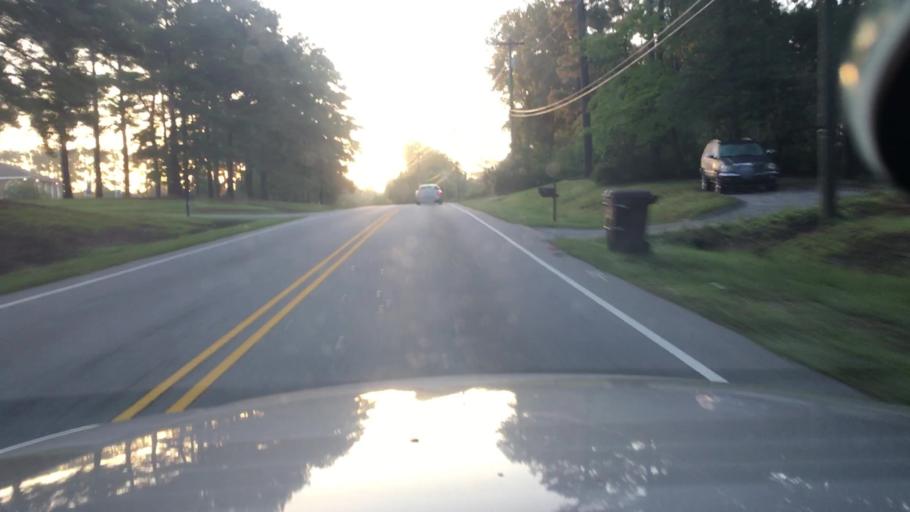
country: US
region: North Carolina
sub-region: Cumberland County
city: Fayetteville
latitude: 35.0615
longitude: -78.9423
